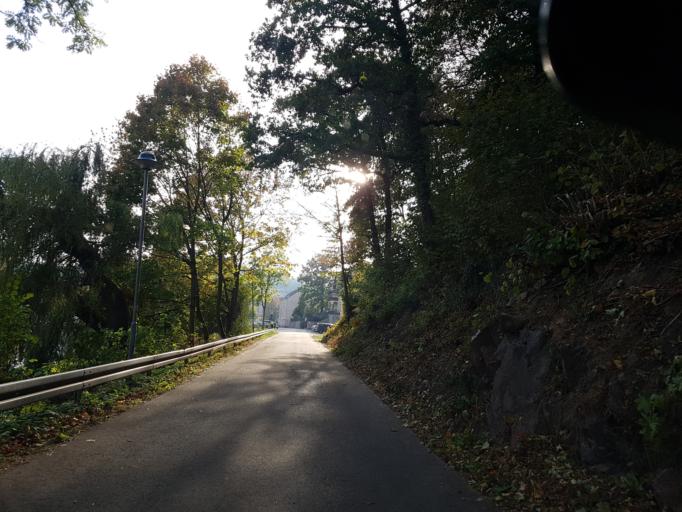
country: DE
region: Saxony
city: Waldheim
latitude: 51.0754
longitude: 13.0249
